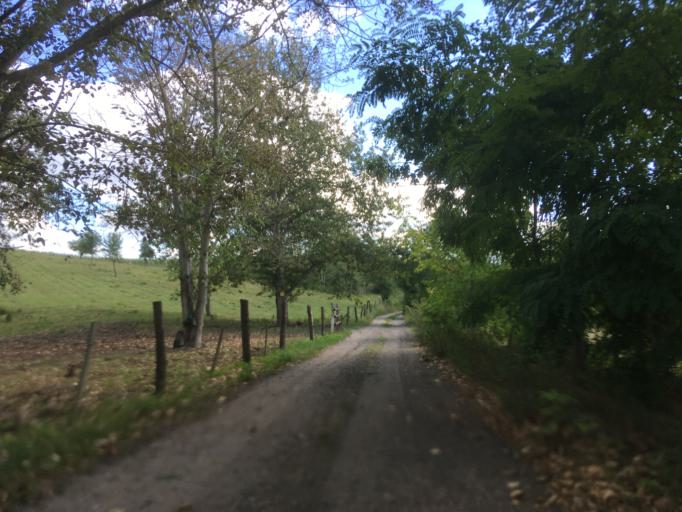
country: DE
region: Brandenburg
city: Angermunde
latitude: 52.9408
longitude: 14.0005
